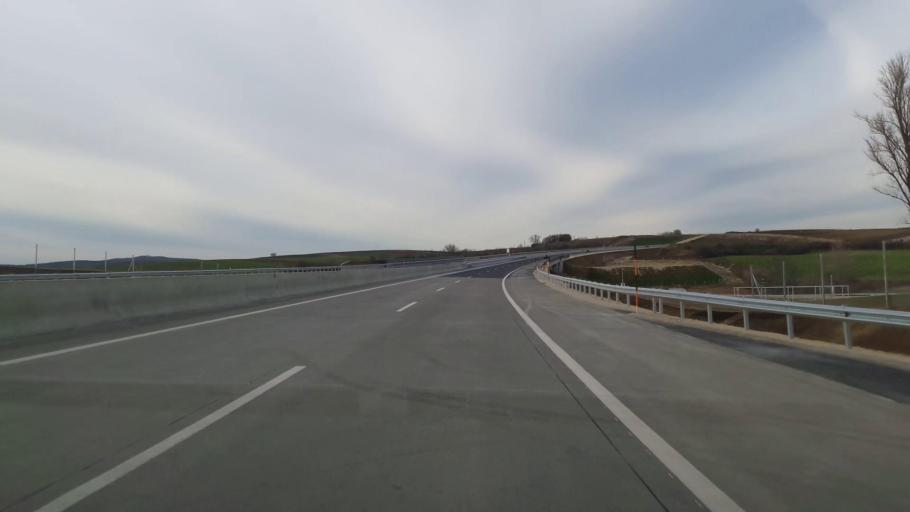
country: AT
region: Lower Austria
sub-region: Politischer Bezirk Mistelbach
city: Herrnbaumgarten
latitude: 48.6814
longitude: 16.6598
